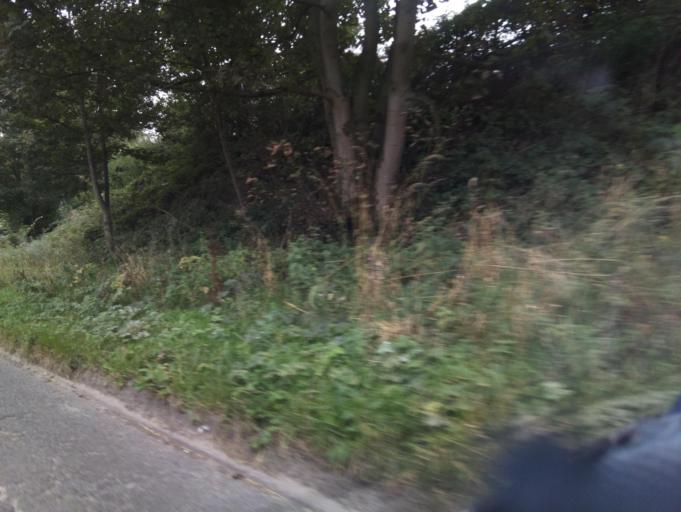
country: GB
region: England
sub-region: Derbyshire
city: Ashbourne
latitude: 53.0138
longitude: -1.7147
